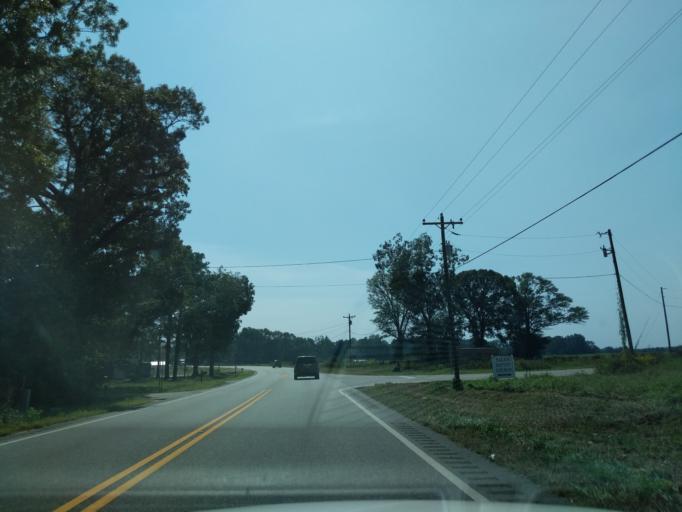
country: US
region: Alabama
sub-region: Covington County
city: Andalusia
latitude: 31.2448
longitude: -86.5269
